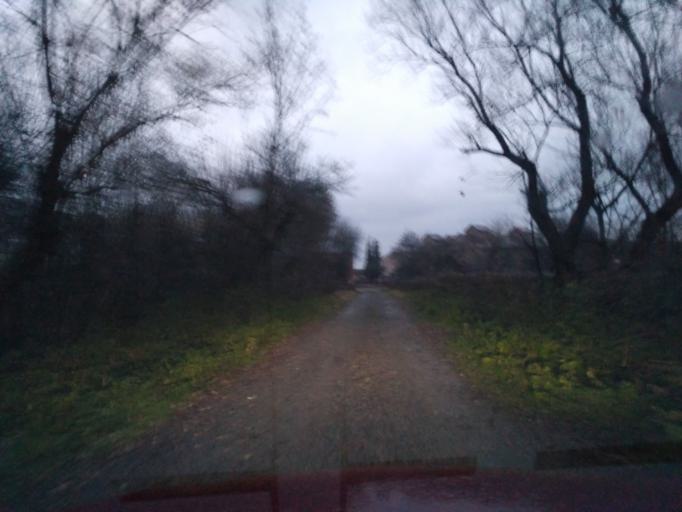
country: SK
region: Kosicky
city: Kosice
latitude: 48.5832
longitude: 21.1681
